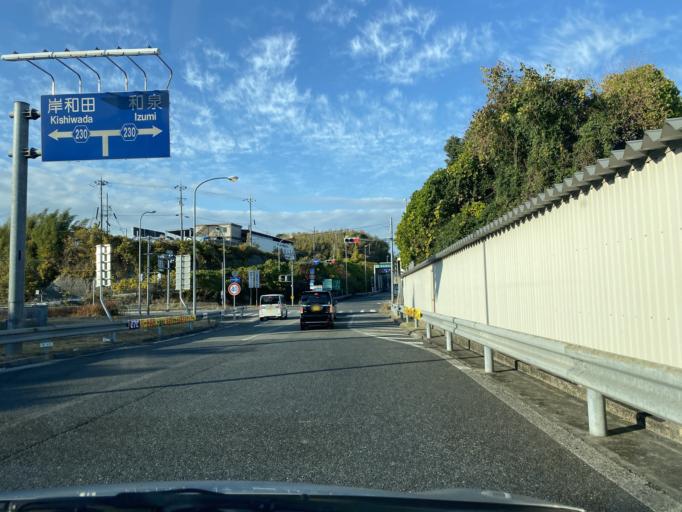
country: JP
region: Osaka
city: Izumi
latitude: 34.4378
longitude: 135.4442
